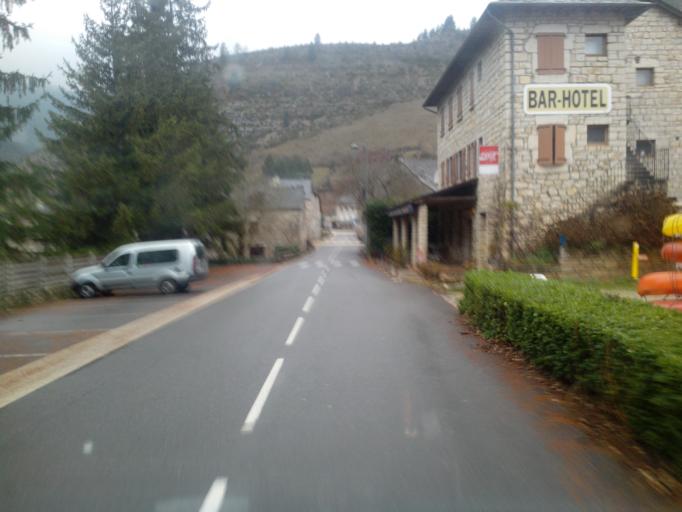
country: FR
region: Languedoc-Roussillon
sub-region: Departement de la Lozere
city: Florac
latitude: 44.3371
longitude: 3.4838
